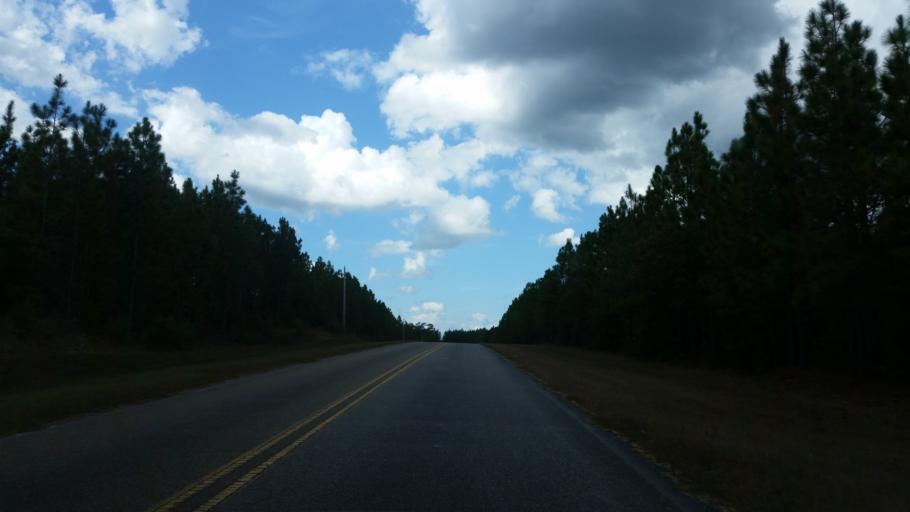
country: US
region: Alabama
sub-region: Escambia County
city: Atmore
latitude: 30.8920
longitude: -87.5458
